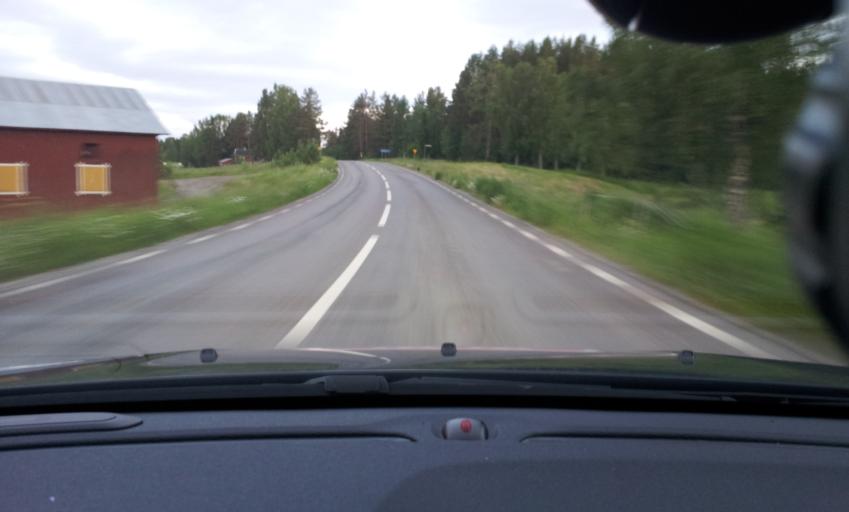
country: SE
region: Jaemtland
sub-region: Ragunda Kommun
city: Hammarstrand
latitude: 63.0959
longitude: 16.3571
